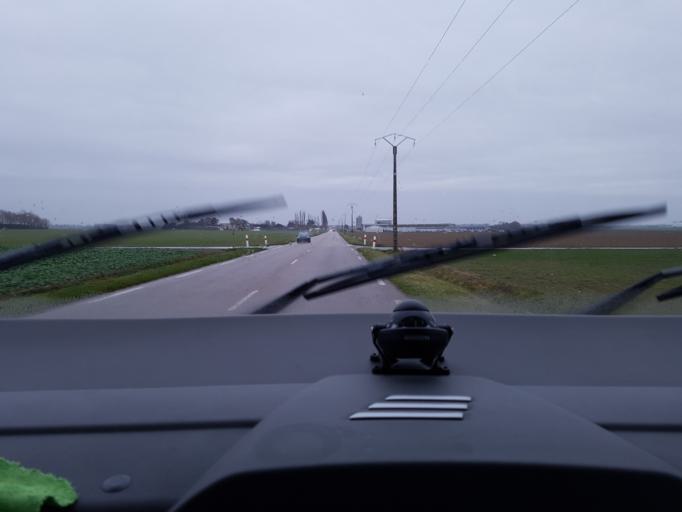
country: FR
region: Haute-Normandie
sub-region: Departement de l'Eure
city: Le Neubourg
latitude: 49.1483
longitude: 0.9290
